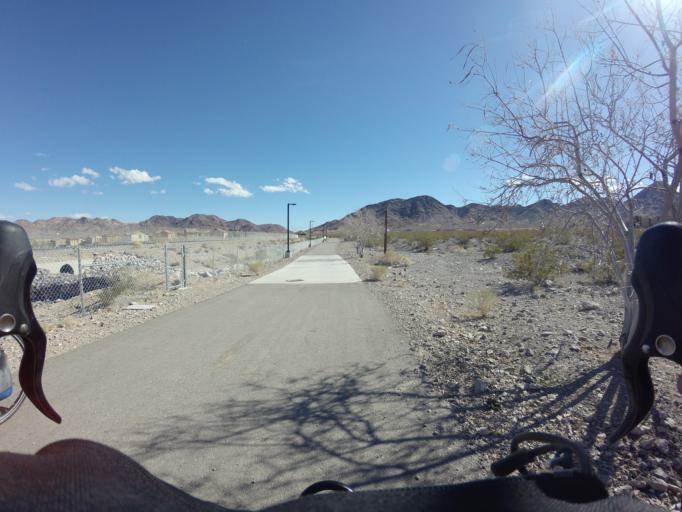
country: US
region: Nevada
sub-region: Clark County
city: Henderson
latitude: 35.9881
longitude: -114.9363
